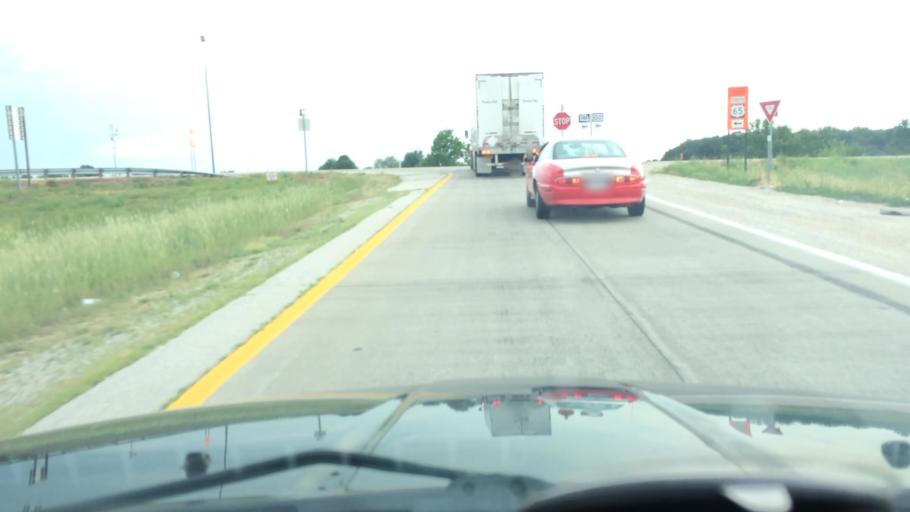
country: US
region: Missouri
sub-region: Greene County
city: Strafford
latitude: 37.2512
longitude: -93.1826
